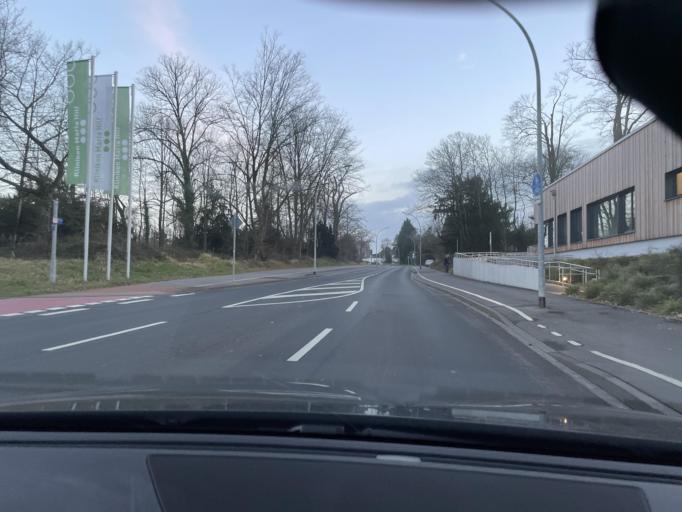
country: DE
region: North Rhine-Westphalia
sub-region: Regierungsbezirk Dusseldorf
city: Monchengladbach
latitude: 51.2180
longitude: 6.4184
